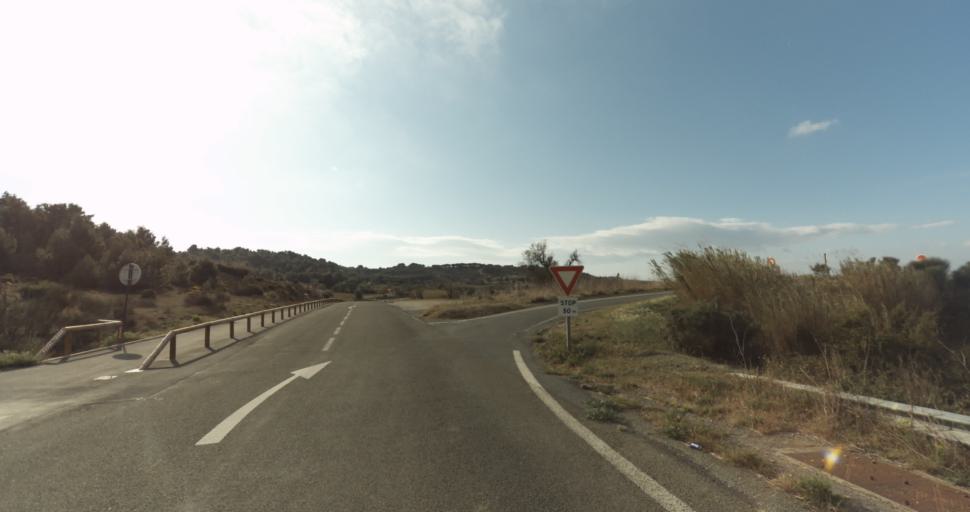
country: FR
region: Languedoc-Roussillon
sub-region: Departement de l'Aude
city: Leucate
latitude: 42.9289
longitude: 3.0112
